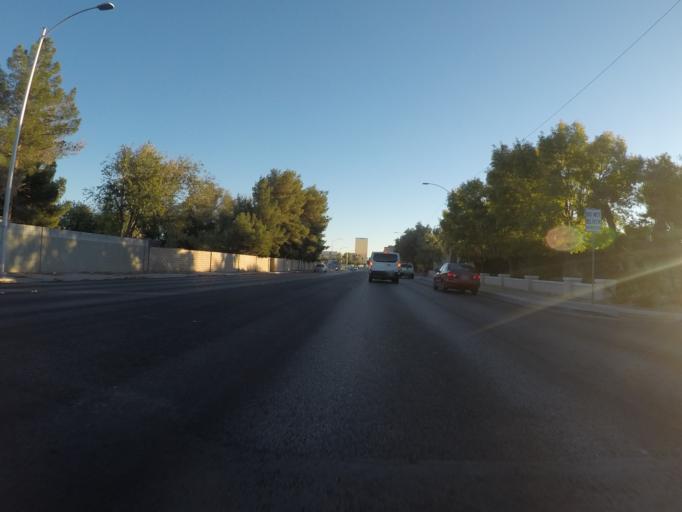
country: US
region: Nevada
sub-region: Clark County
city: Las Vegas
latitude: 36.1537
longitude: -115.1730
